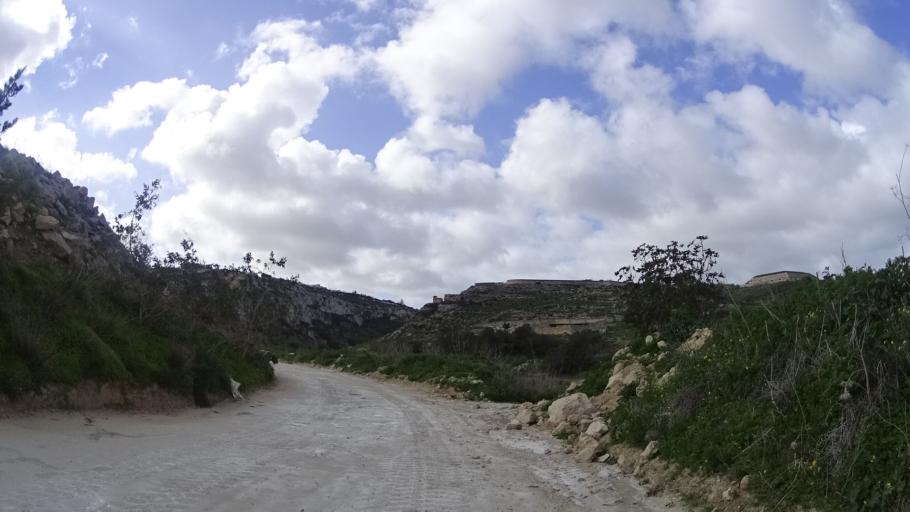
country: MT
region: In-Naxxar
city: Naxxar
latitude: 35.9241
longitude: 14.4327
